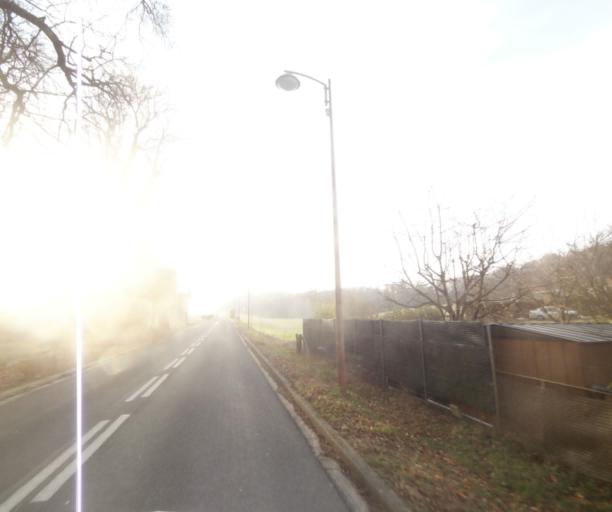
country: FR
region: Champagne-Ardenne
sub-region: Departement de la Haute-Marne
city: Chancenay
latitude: 48.7217
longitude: 4.9419
